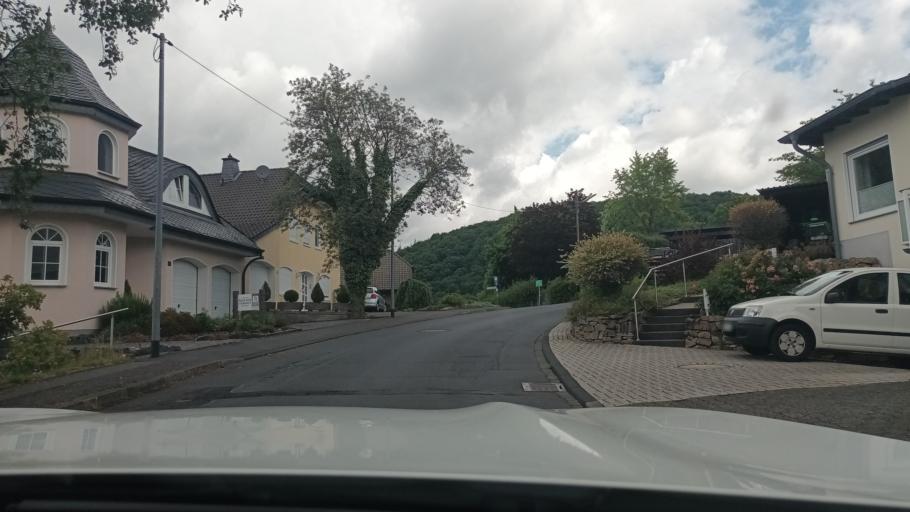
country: DE
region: Rheinland-Pfalz
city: Kircheib
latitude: 50.7339
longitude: 7.4522
